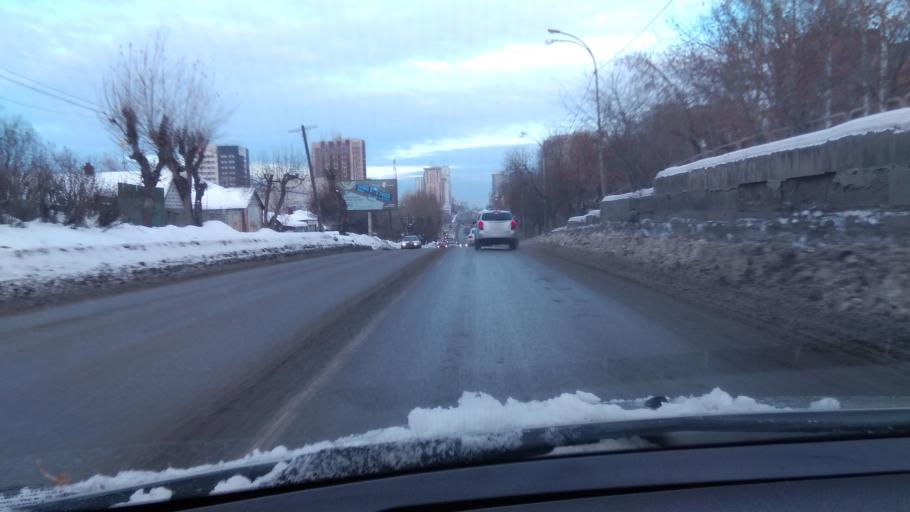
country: RU
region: Sverdlovsk
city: Yekaterinburg
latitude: 56.8093
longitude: 60.5916
